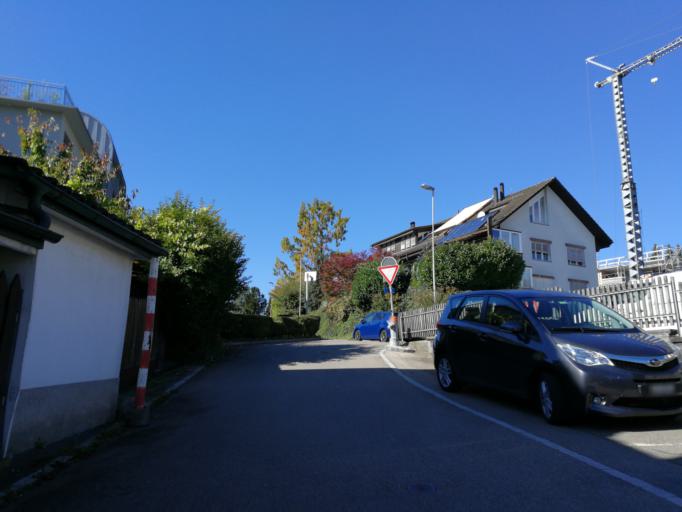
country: CH
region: Zurich
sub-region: Bezirk Meilen
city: Stafa
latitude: 47.2490
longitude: 8.7192
